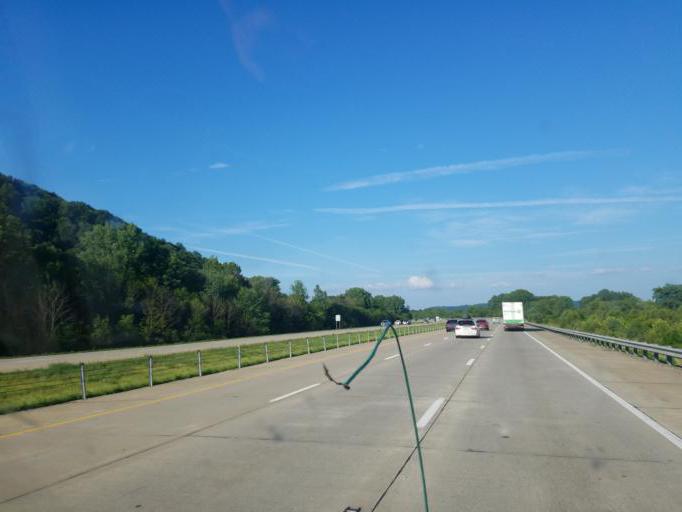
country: US
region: Kentucky
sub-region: Bullitt County
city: Lebanon Junction
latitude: 37.7892
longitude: -85.7635
